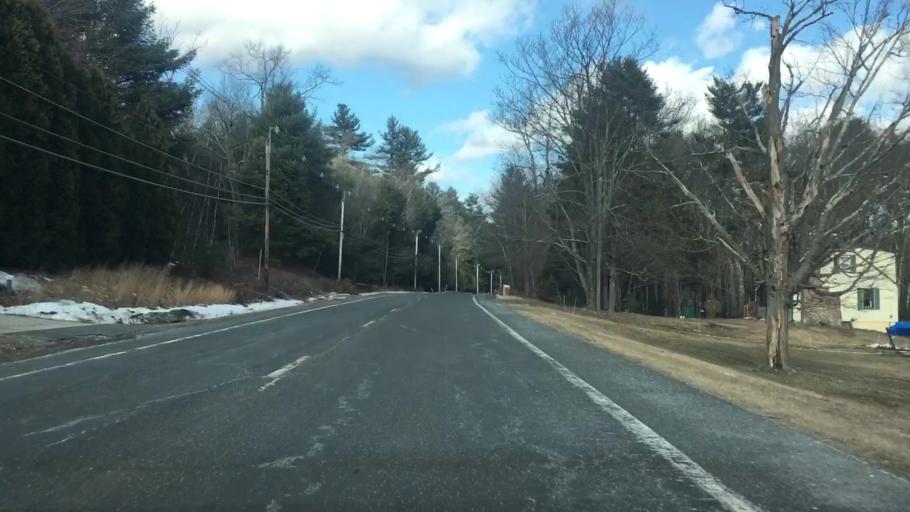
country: US
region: Massachusetts
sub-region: Hampden County
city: Brimfield
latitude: 42.0959
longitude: -72.2017
